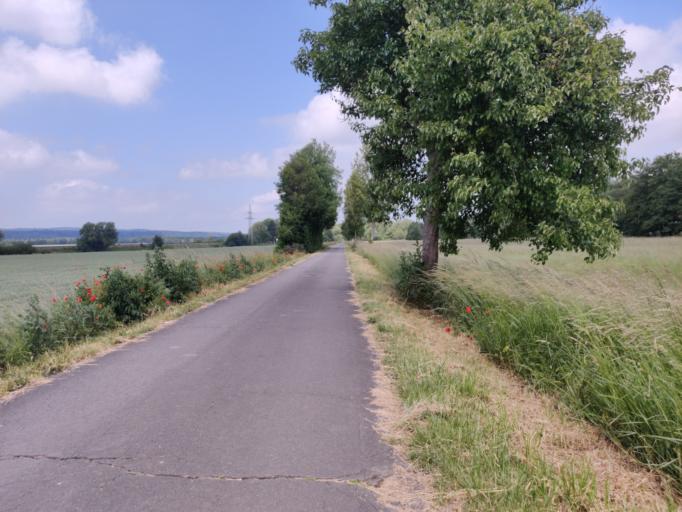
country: DE
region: Lower Saxony
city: Hildesheim
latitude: 52.1220
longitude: 9.9717
